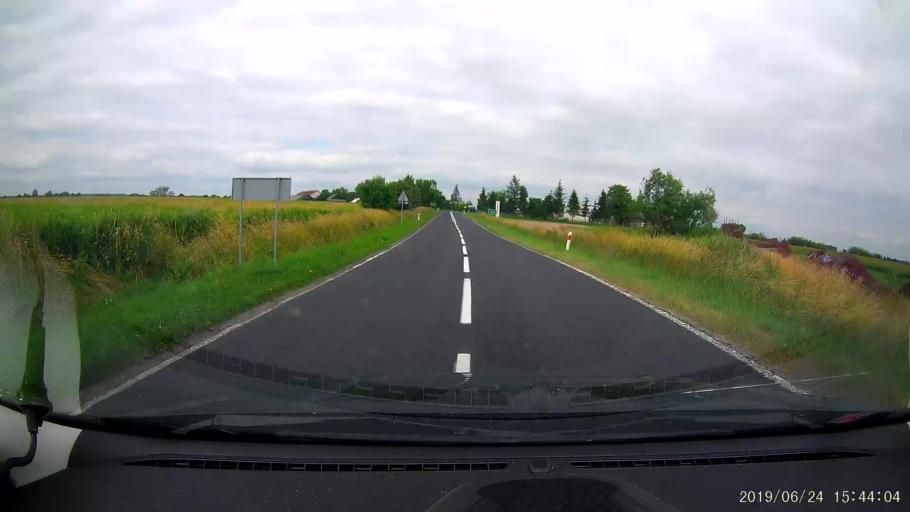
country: PL
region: Subcarpathian Voivodeship
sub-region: Powiat lubaczowski
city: Oleszyce
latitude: 50.1355
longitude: 22.9563
